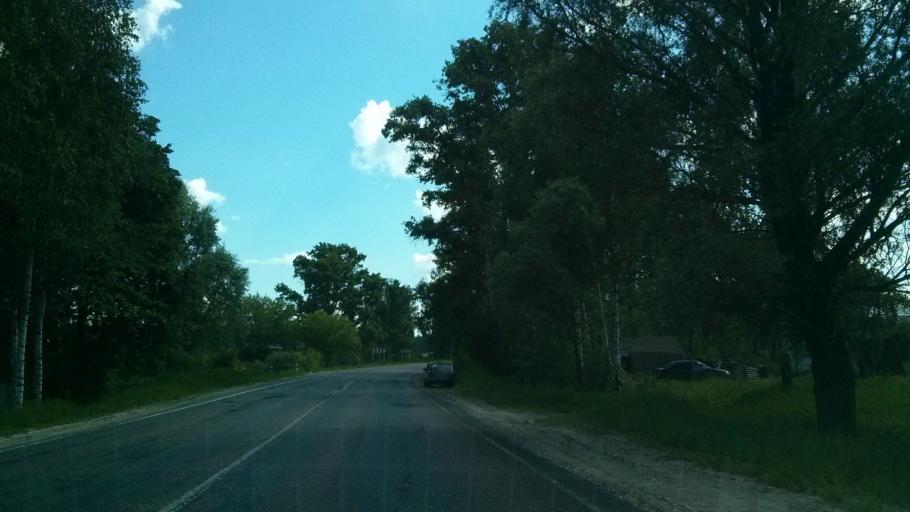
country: RU
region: Vladimir
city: Murom
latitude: 55.4739
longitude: 41.8913
